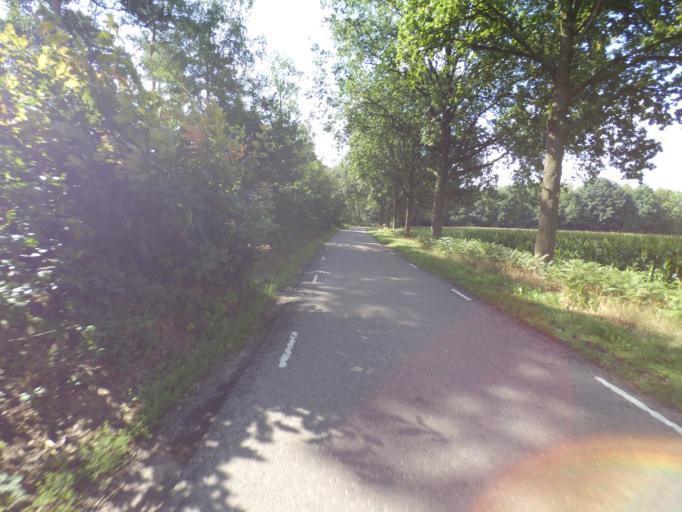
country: NL
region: Limburg
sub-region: Gemeente Echt-Susteren
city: Koningsbosch
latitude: 51.0753
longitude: 5.9258
